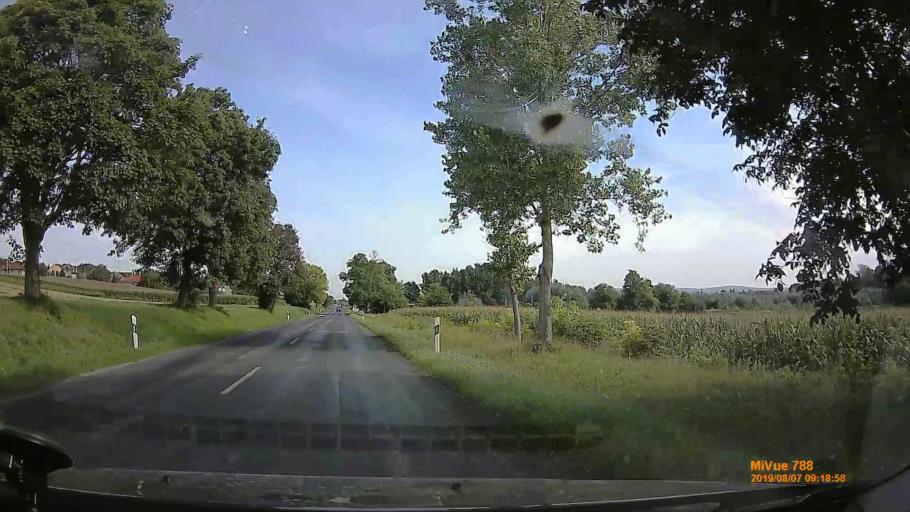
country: HU
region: Zala
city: Sarmellek
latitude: 46.7483
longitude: 17.1754
